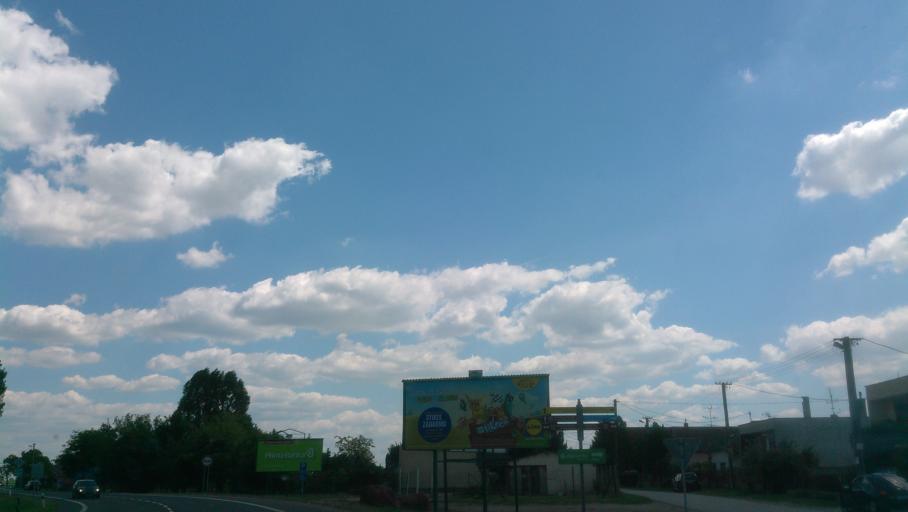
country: SK
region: Trnavsky
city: Dunajska Streda
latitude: 47.9484
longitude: 17.7100
